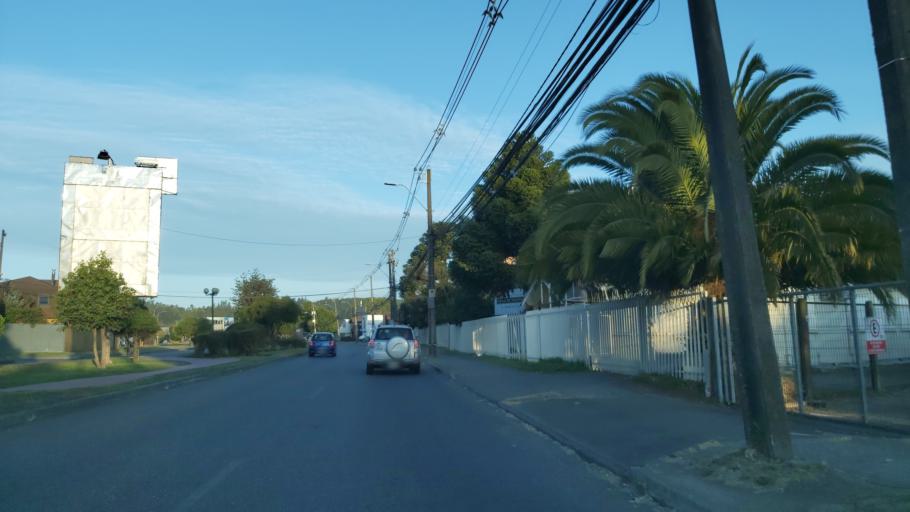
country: CL
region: Biobio
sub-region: Provincia de Concepcion
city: Concepcion
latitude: -36.8442
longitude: -73.0980
